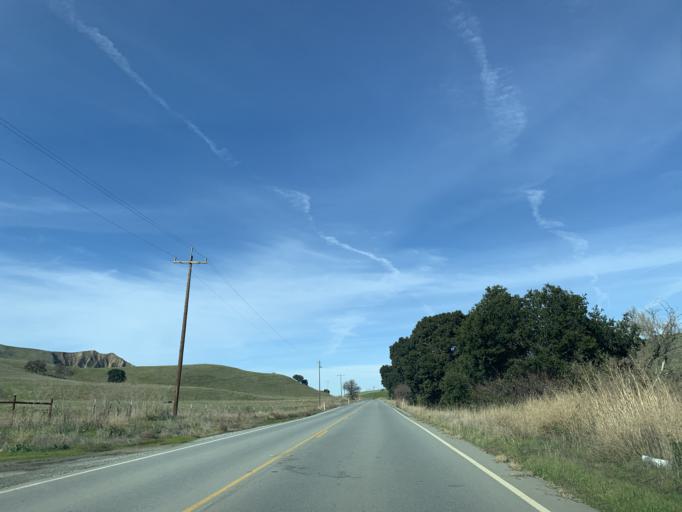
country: US
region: California
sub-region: San Benito County
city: Ridgemark
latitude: 36.7489
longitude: -121.2866
